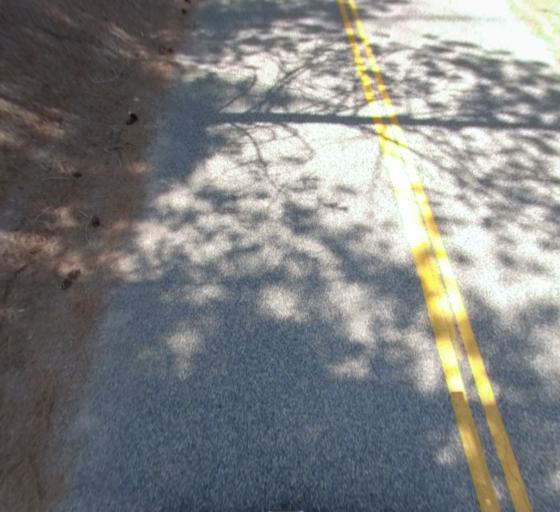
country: US
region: California
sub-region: Madera County
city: Oakhurst
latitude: 37.4097
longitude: -119.3477
